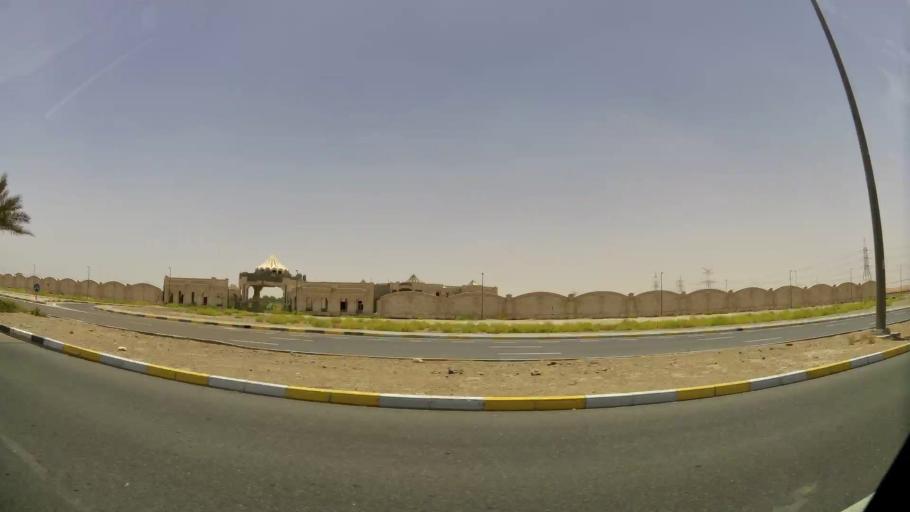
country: OM
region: Al Buraimi
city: Al Buraymi
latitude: 24.2721
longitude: 55.7206
